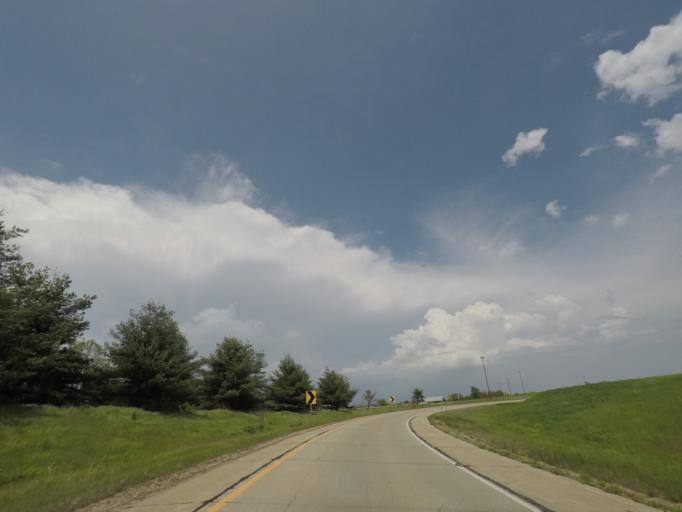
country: US
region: Illinois
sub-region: McLean County
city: Normal
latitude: 40.5377
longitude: -89.0095
